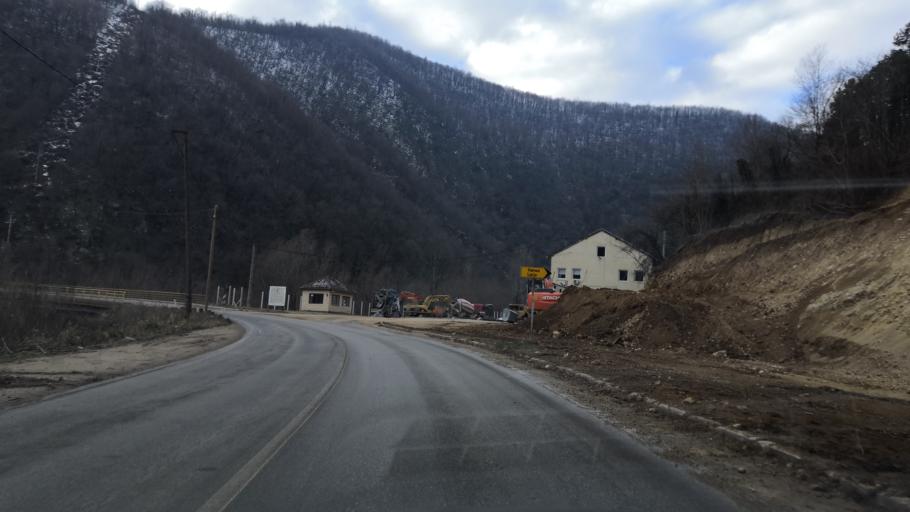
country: RS
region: Central Serbia
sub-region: Macvanski Okrug
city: Mali Zvornik
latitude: 44.3548
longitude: 19.1063
